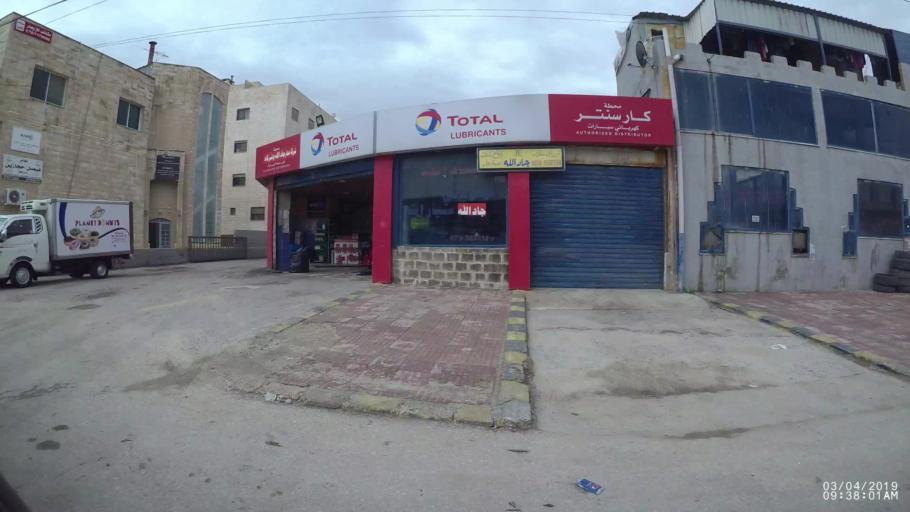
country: JO
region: Amman
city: Wadi as Sir
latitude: 31.9471
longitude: 35.8399
